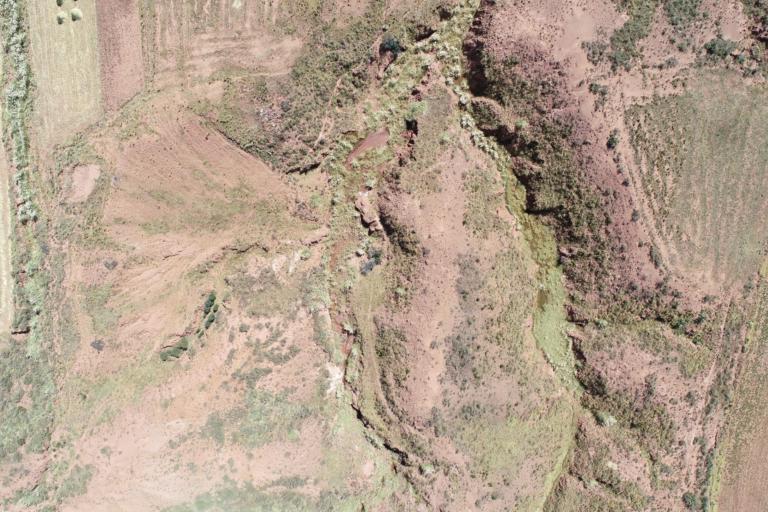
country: BO
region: La Paz
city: Tiahuanaco
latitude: -16.5974
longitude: -68.7544
